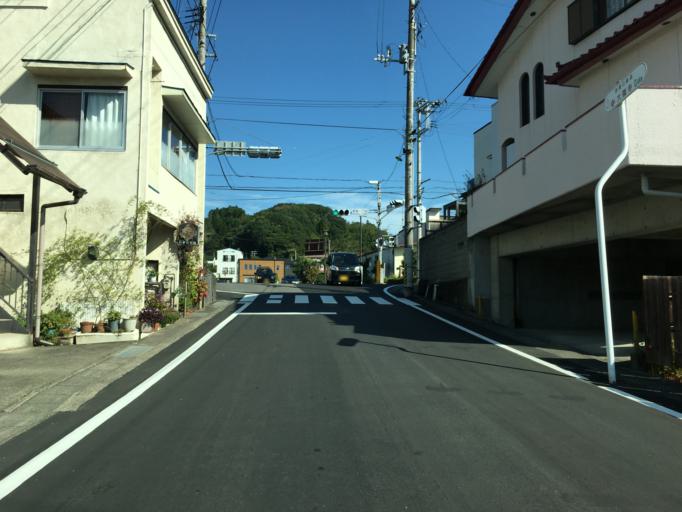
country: JP
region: Fukushima
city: Nihommatsu
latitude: 37.5911
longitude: 140.4274
